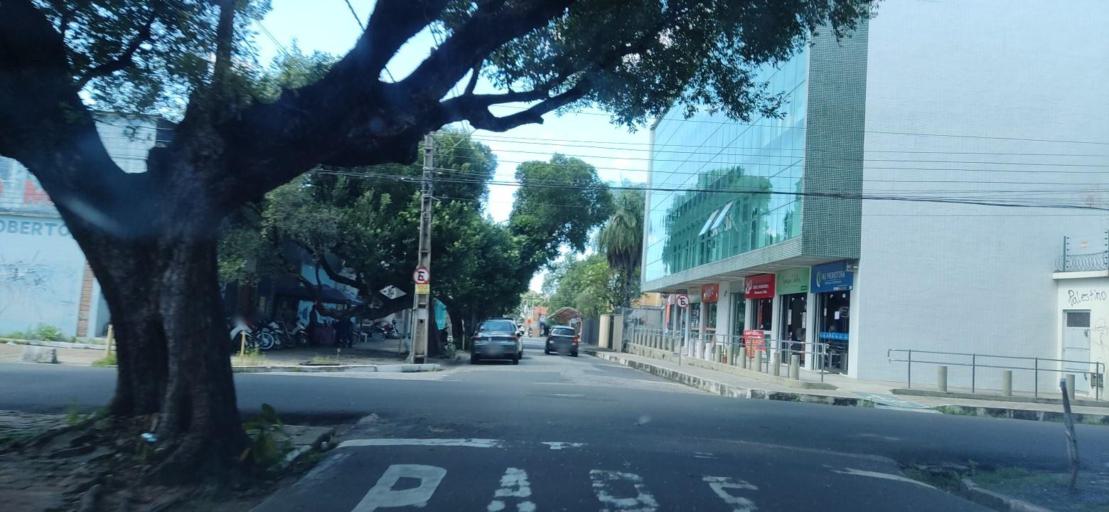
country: BR
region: Piaui
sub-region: Teresina
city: Teresina
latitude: -5.0878
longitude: -42.8137
